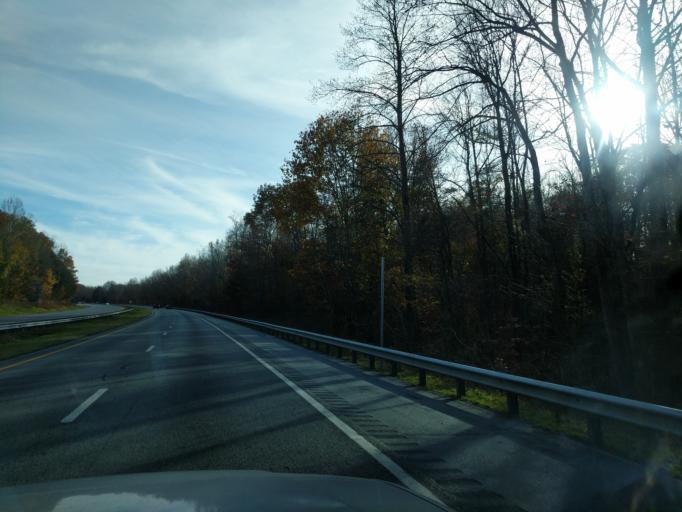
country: US
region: North Carolina
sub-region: Polk County
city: Columbus
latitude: 35.2403
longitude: -82.2049
